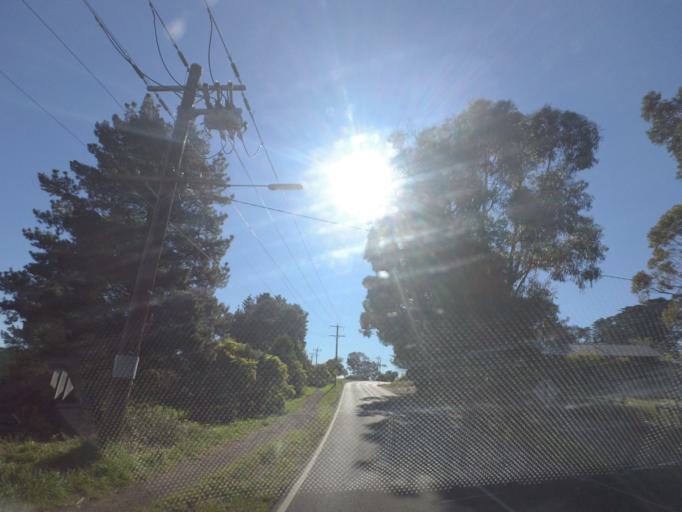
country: AU
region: Victoria
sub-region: Maroondah
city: Croydon Hills
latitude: -37.7457
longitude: 145.2695
